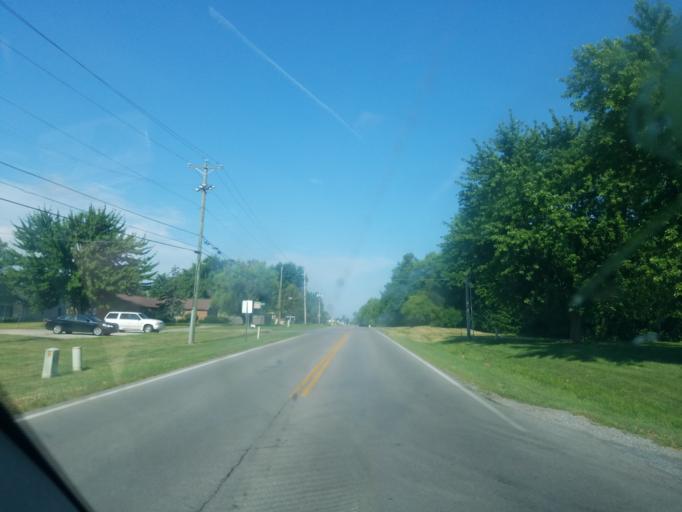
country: US
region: Ohio
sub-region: Allen County
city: Lima
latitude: 40.7455
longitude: -84.0583
